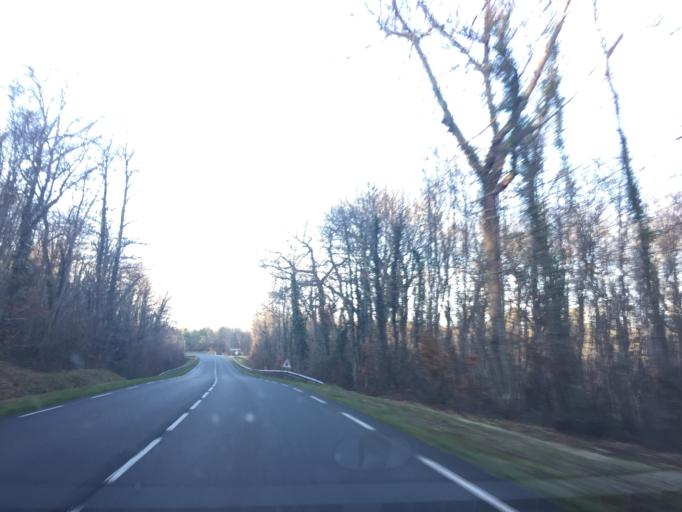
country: FR
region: Aquitaine
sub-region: Departement de la Dordogne
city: Riberac
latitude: 45.1835
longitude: 0.3828
